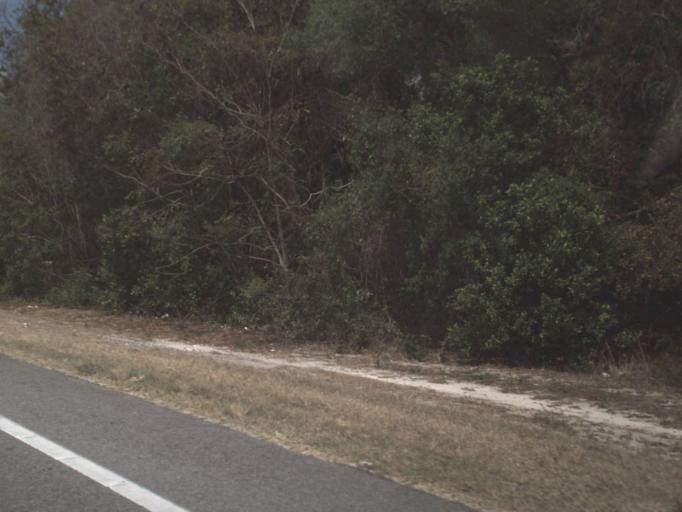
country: US
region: Florida
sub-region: Lake County
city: Mascotte
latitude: 28.5778
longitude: -81.9169
